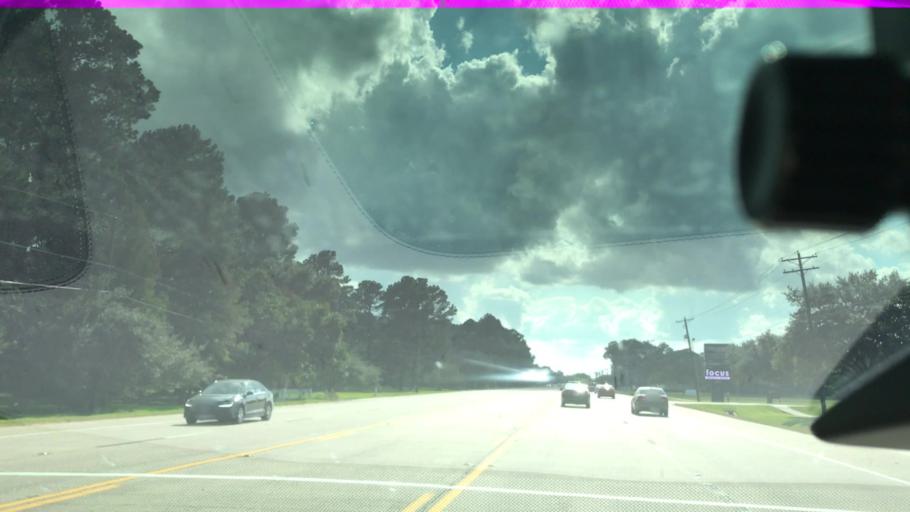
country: US
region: Texas
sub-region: Harris County
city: Webster
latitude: 29.4927
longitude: -95.1466
